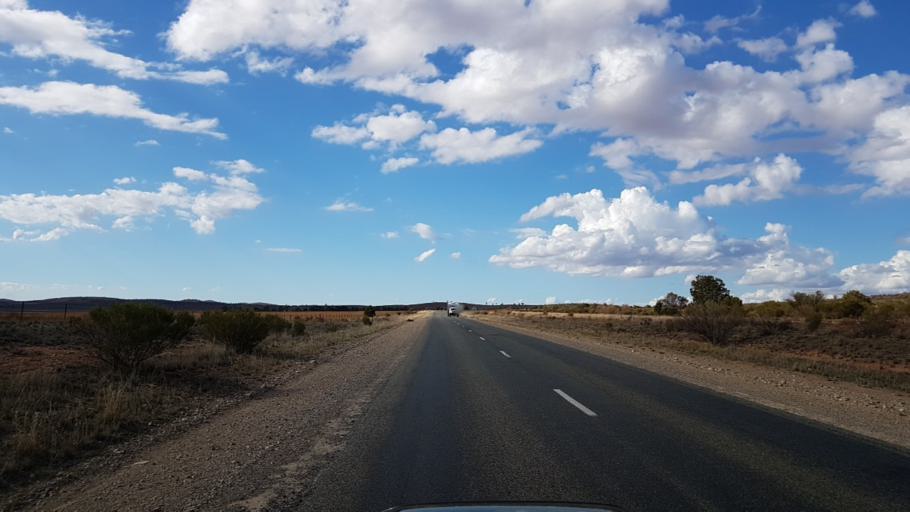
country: AU
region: South Australia
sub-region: Peterborough
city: Peterborough
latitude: -32.9593
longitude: 138.8924
